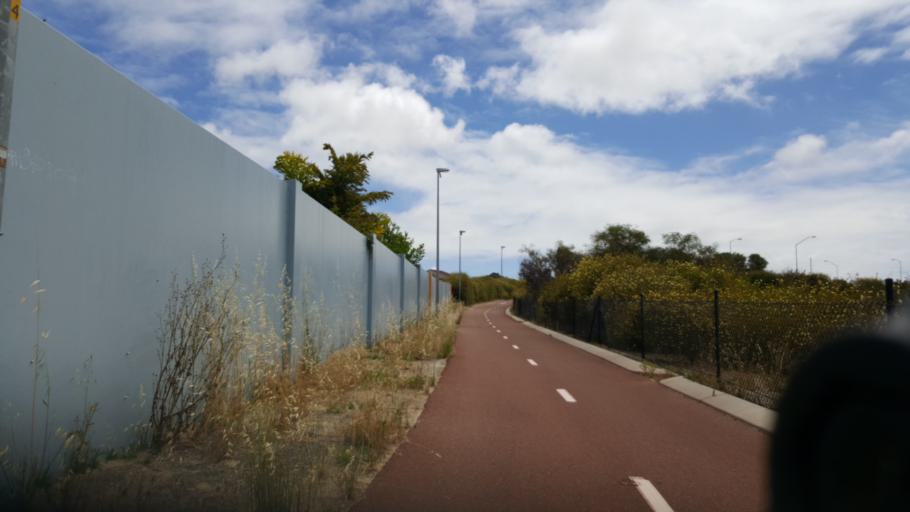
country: AU
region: Western Australia
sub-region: Bayswater
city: Embleton
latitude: -31.8688
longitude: 115.8844
